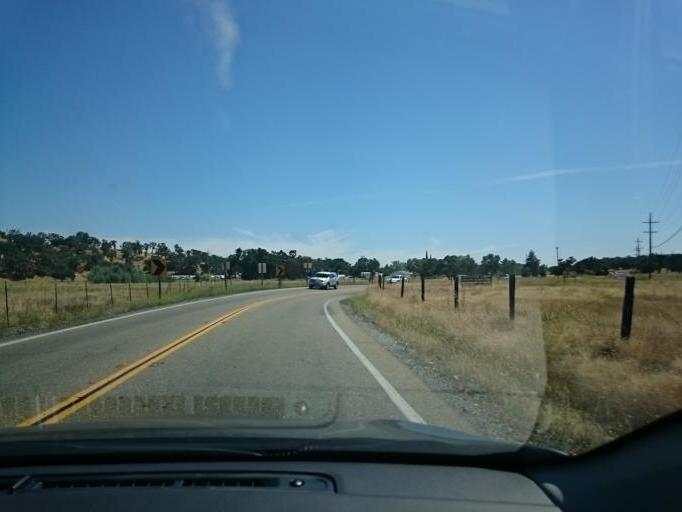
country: US
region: California
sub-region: Calaveras County
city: Valley Springs
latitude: 38.1837
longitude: -120.8259
